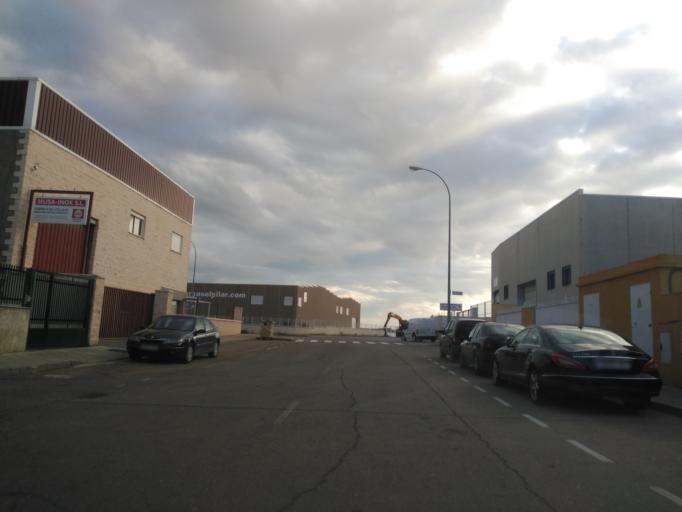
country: ES
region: Castille and Leon
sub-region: Provincia de Salamanca
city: Carbajosa de la Sagrada
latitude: 40.9374
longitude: -5.6604
